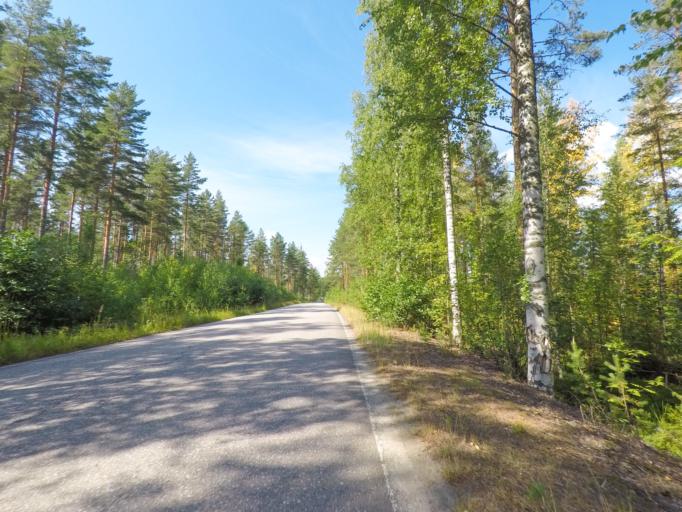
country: FI
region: Southern Savonia
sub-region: Mikkeli
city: Puumala
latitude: 61.4698
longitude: 28.1681
